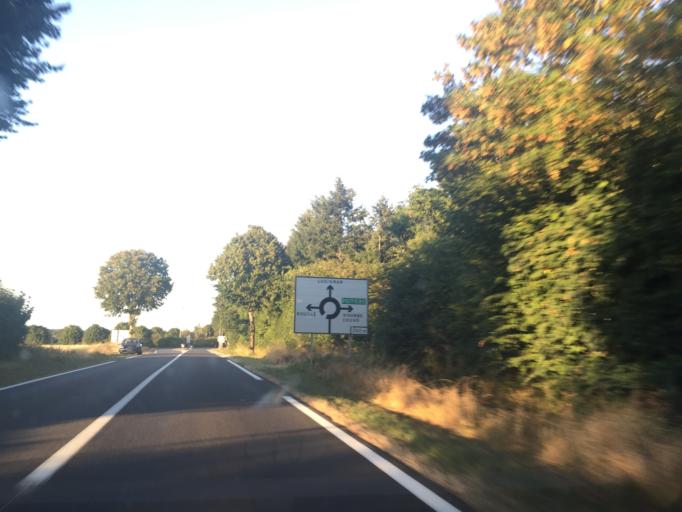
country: FR
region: Poitou-Charentes
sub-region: Departement de la Vienne
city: Lusignan
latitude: 46.4250
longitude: 0.1103
